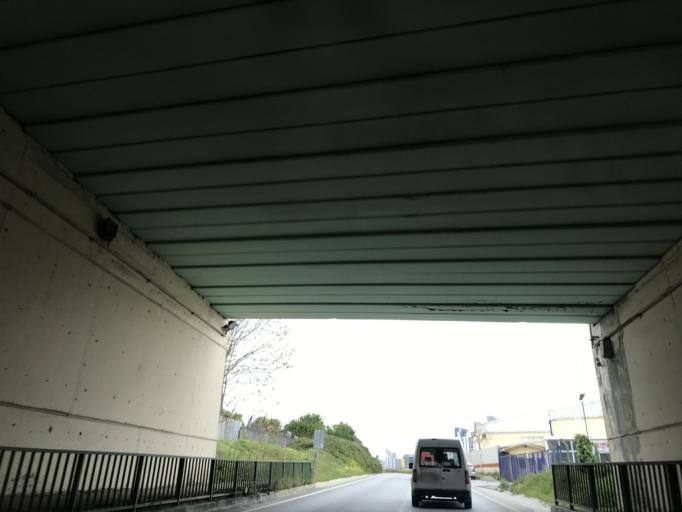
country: TR
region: Istanbul
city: Maltepe
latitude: 40.9039
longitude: 29.2089
